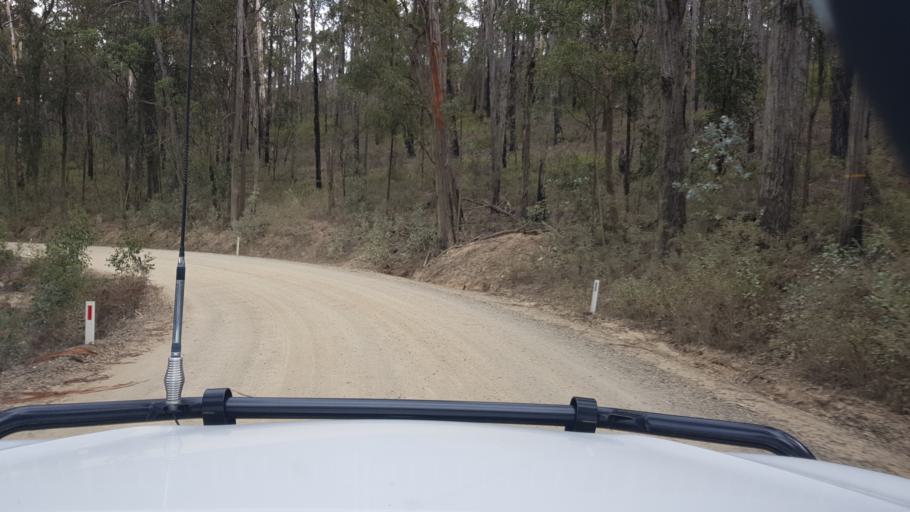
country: AU
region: Victoria
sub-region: East Gippsland
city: Bairnsdale
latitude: -37.6966
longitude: 147.5738
